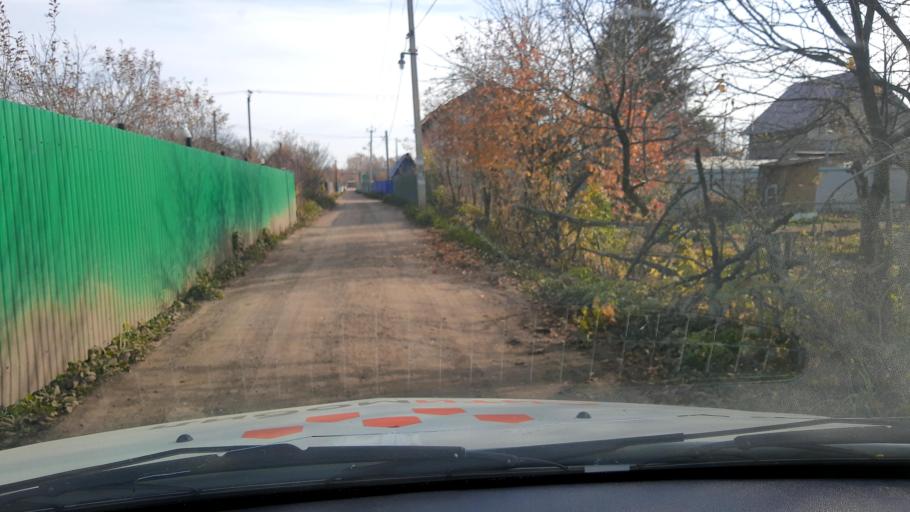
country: RU
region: Bashkortostan
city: Ufa
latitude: 54.8111
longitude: 56.1527
